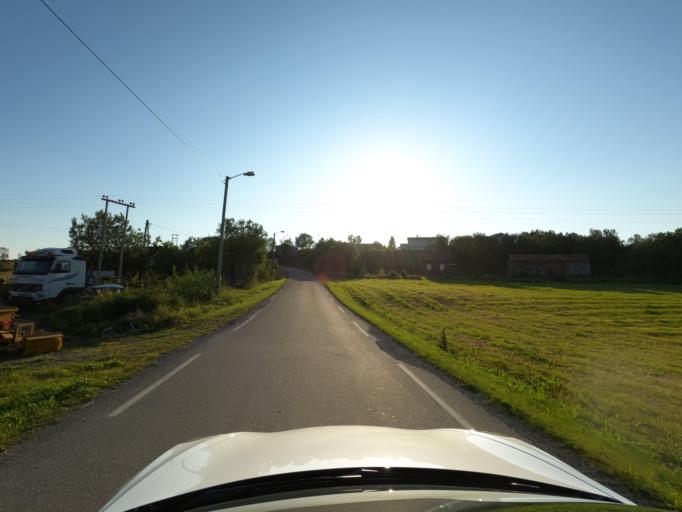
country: NO
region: Troms
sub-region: Skanland
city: Evenskjer
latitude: 68.4640
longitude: 16.6446
